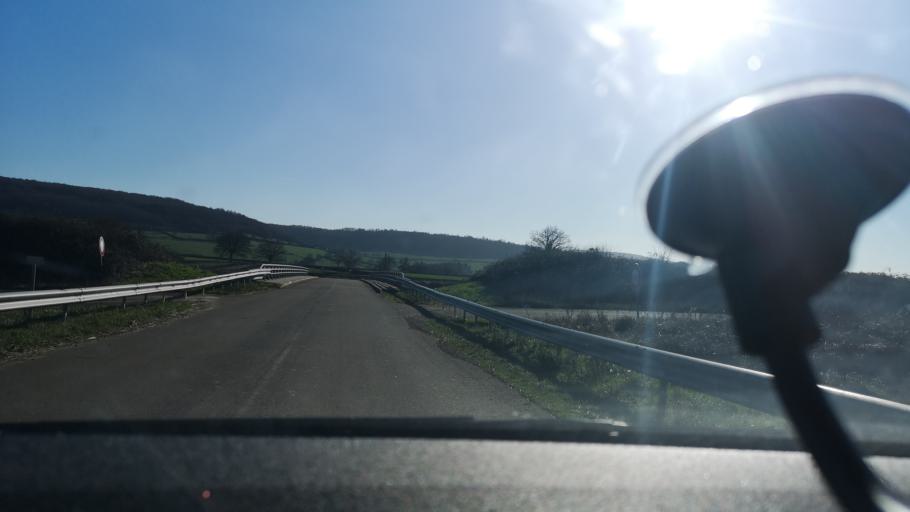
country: FR
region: Bourgogne
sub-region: Departement de Saone-et-Loire
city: Buxy
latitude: 46.7424
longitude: 4.6351
